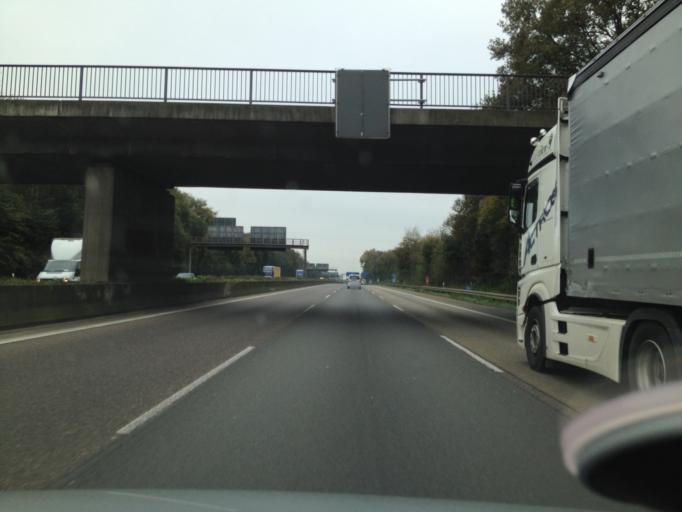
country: DE
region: North Rhine-Westphalia
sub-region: Regierungsbezirk Koln
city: Ostheim
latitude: 50.9198
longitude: 7.0446
